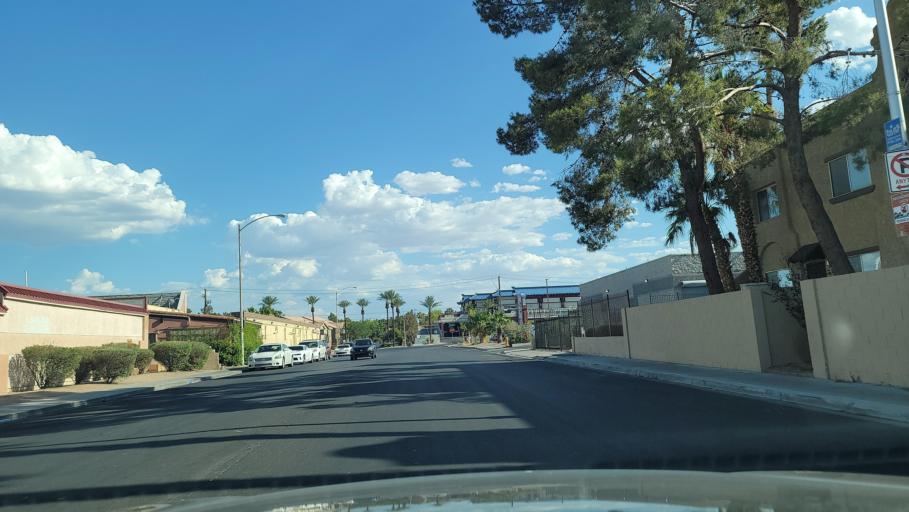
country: US
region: Nevada
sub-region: Clark County
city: Spring Valley
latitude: 36.1276
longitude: -115.2102
